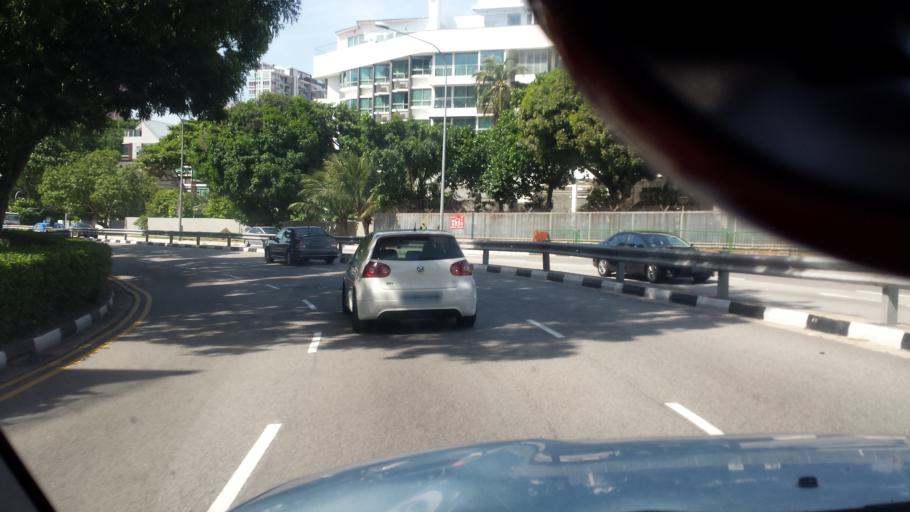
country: SG
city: Singapore
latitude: 1.3123
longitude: 103.8908
